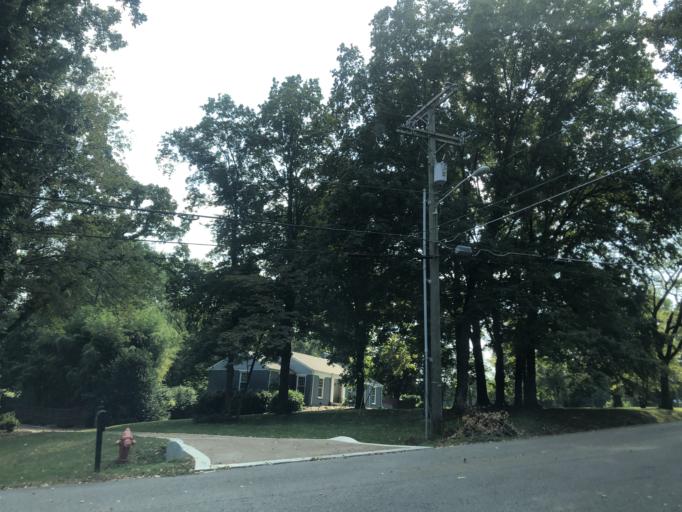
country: US
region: Tennessee
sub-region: Davidson County
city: Oak Hill
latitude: 36.0999
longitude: -86.7797
